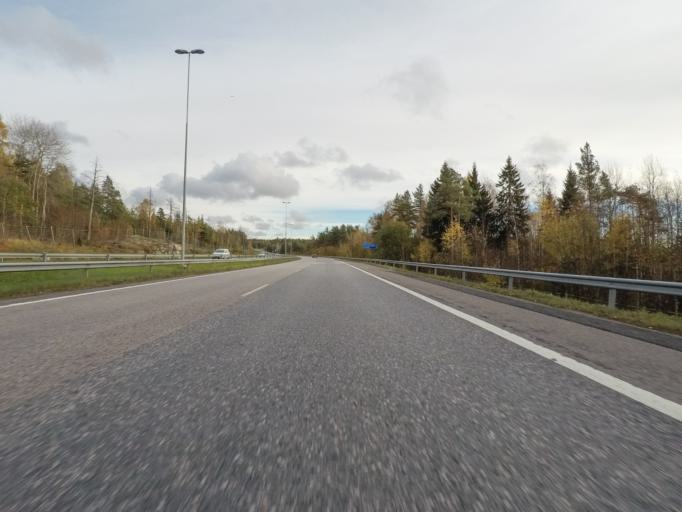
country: FI
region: Uusimaa
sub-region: Helsinki
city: Sibbo
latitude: 60.2649
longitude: 25.1978
